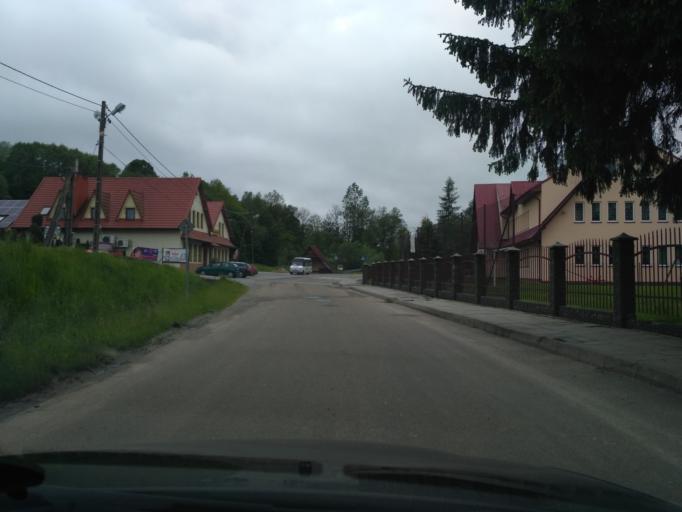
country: PL
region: Subcarpathian Voivodeship
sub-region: Powiat jasielski
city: Brzyska
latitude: 49.8504
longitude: 21.3732
